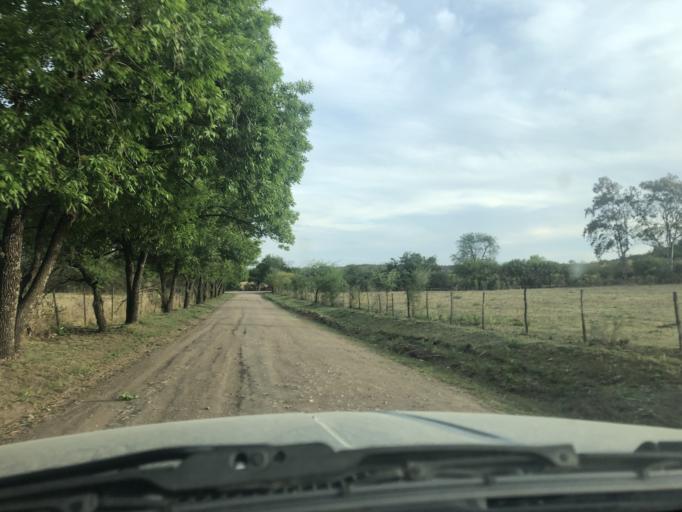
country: AR
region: Cordoba
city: La Granja
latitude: -31.0161
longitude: -64.2516
